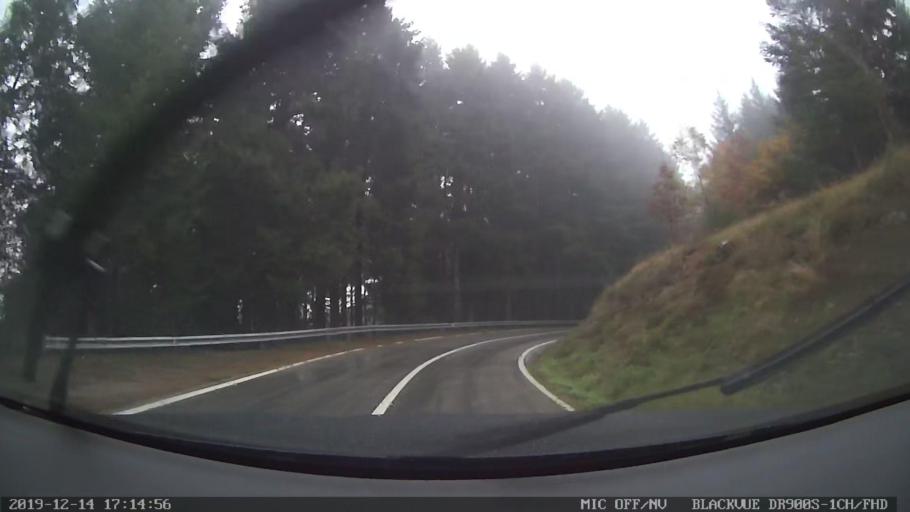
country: PT
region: Vila Real
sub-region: Vila Pouca de Aguiar
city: Vila Pouca de Aguiar
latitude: 41.5025
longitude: -7.6291
